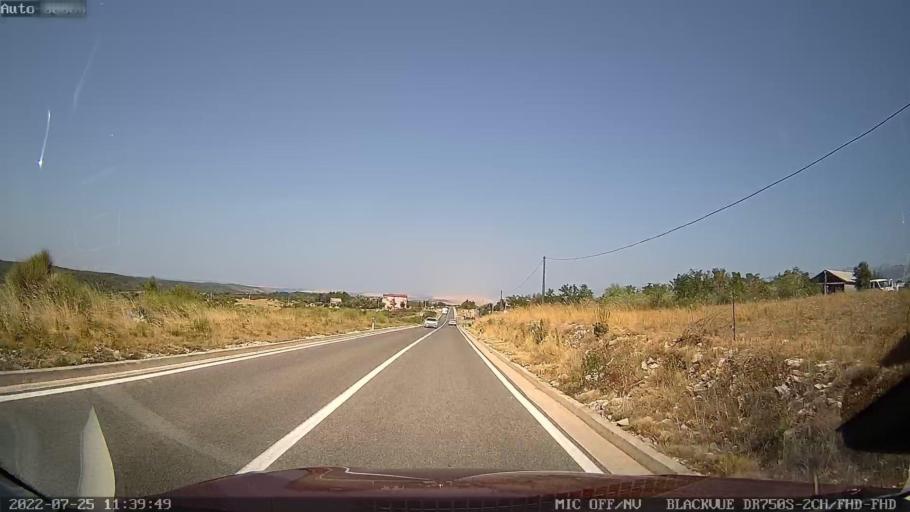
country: HR
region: Zadarska
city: Razanac
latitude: 44.2591
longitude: 15.3674
